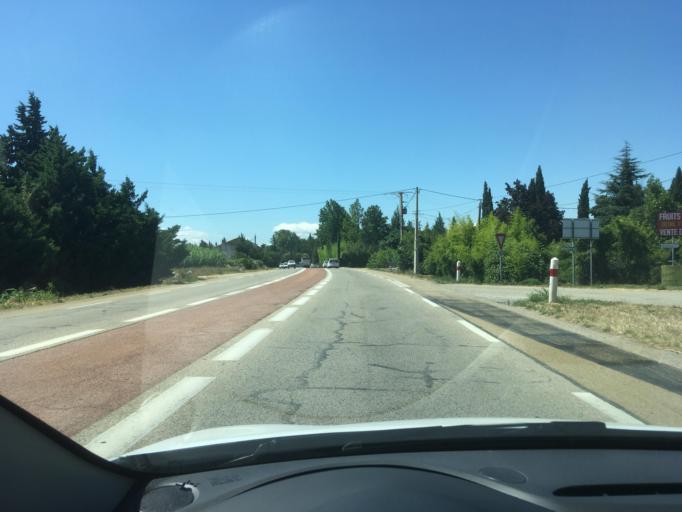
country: FR
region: Provence-Alpes-Cote d'Azur
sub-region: Departement des Bouches-du-Rhone
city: Chateaurenard
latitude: 43.8907
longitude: 4.8334
